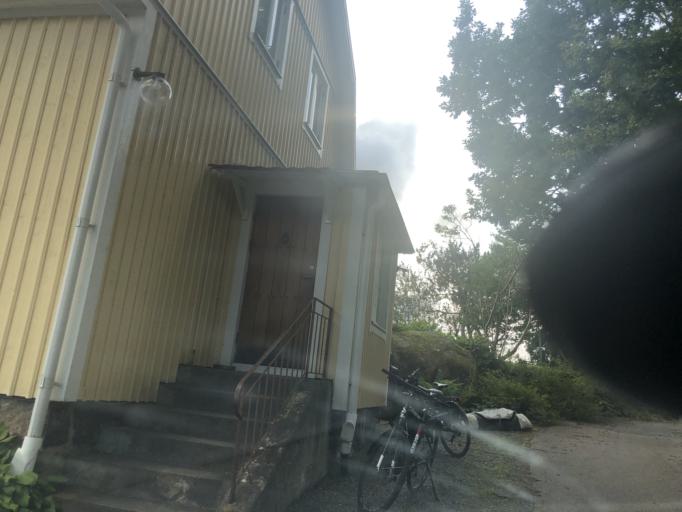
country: SE
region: Vaestra Goetaland
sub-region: Goteborg
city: Goeteborg
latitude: 57.7460
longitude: 11.9543
